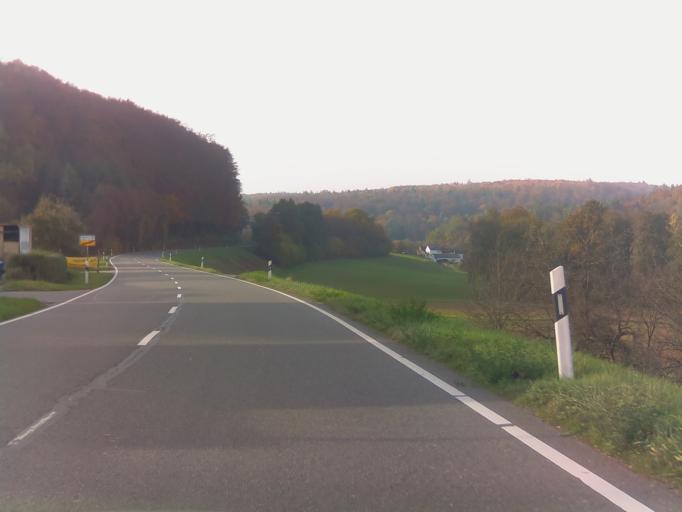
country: DE
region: Baden-Wuerttemberg
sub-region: Karlsruhe Region
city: Billigheim
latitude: 49.3989
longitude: 9.2188
